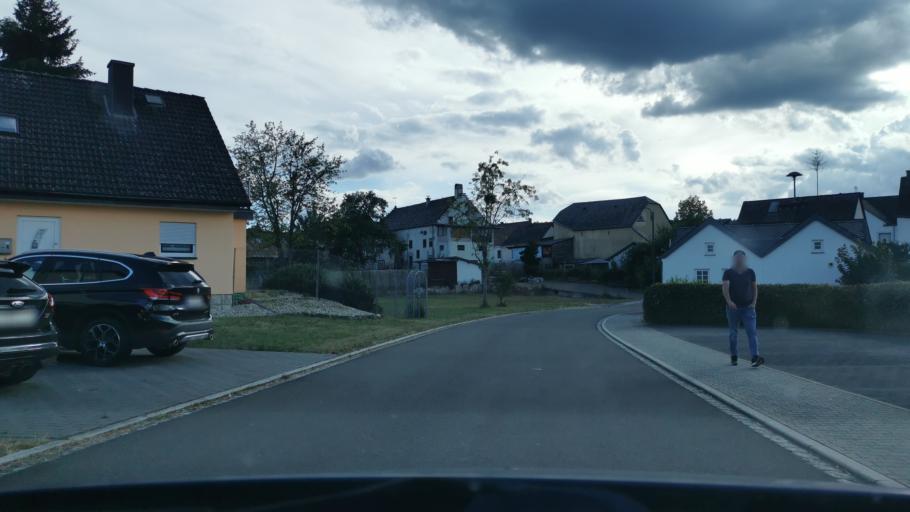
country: DE
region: Rheinland-Pfalz
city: Niersbach
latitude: 49.9310
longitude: 6.7498
